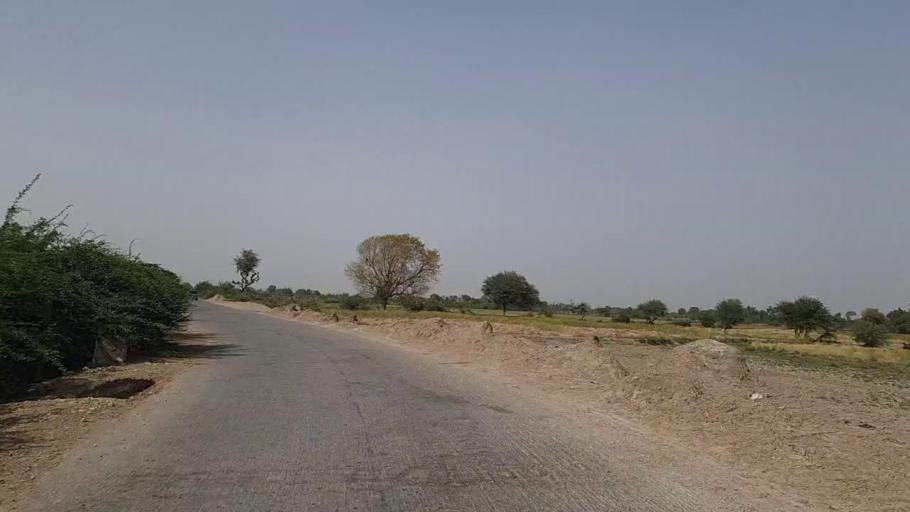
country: PK
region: Sindh
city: Tando Bago
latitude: 24.8938
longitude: 69.0784
